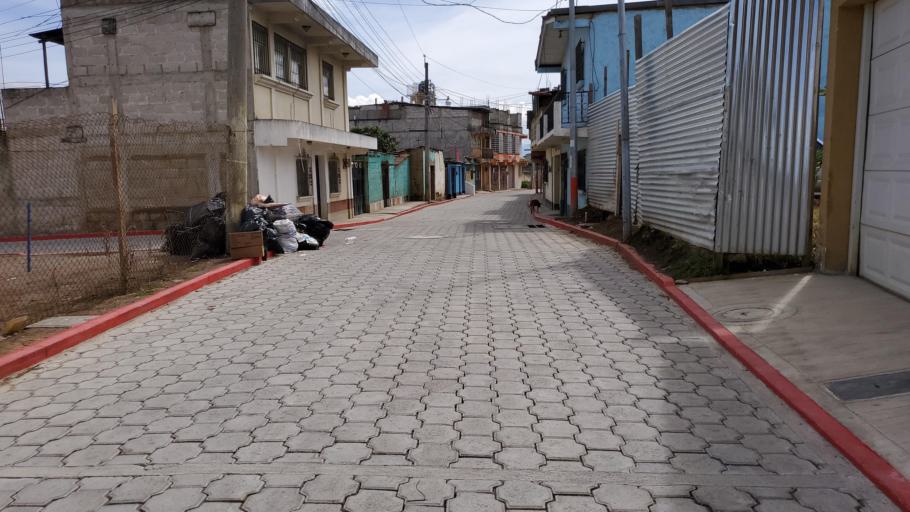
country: GT
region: Quetzaltenango
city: Quetzaltenango
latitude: 14.8385
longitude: -91.5370
